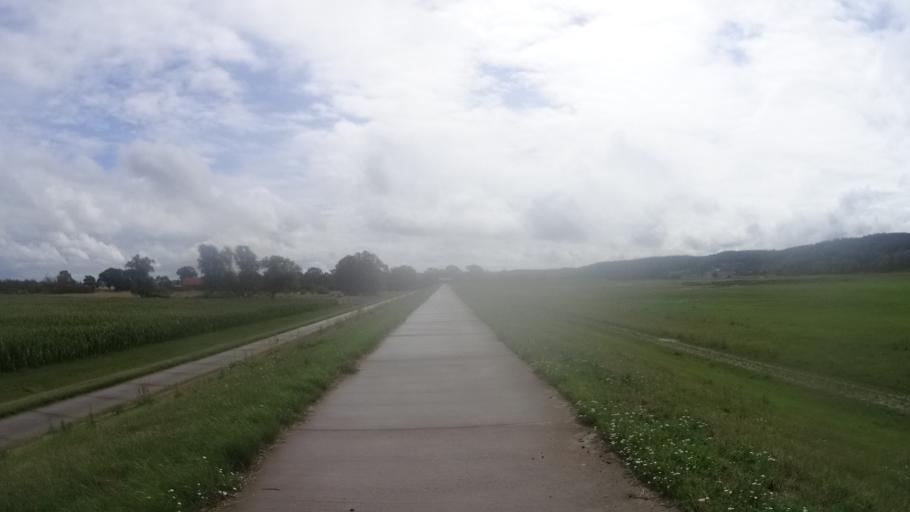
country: DE
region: Lower Saxony
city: Neu Darchau
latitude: 53.2277
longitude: 10.9314
